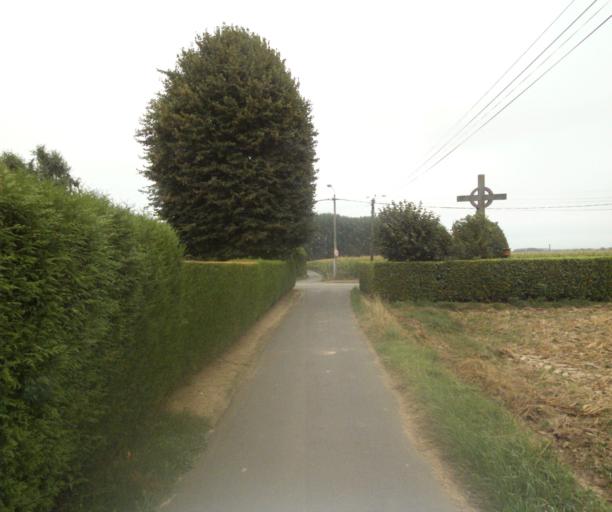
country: FR
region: Nord-Pas-de-Calais
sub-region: Departement du Nord
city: Sailly-lez-Lannoy
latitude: 50.6445
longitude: 3.2156
